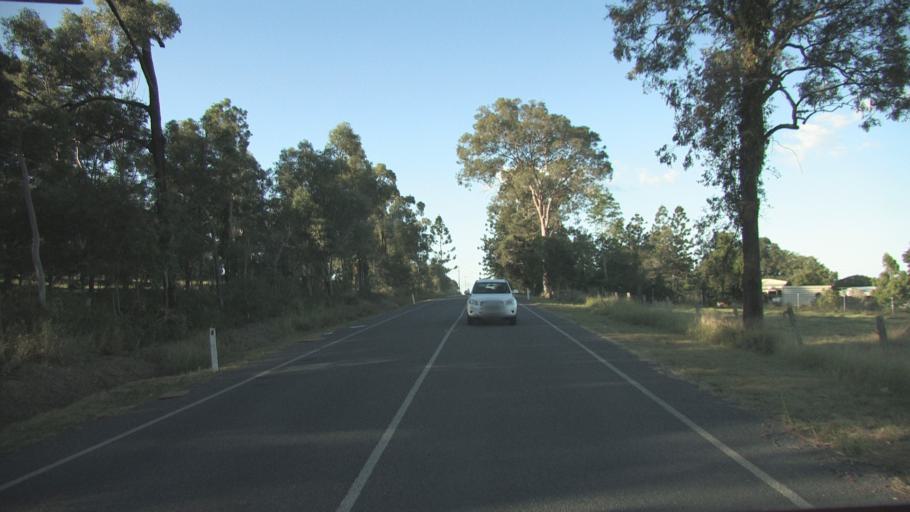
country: AU
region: Queensland
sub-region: Logan
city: Logan Reserve
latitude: -27.7203
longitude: 153.1106
